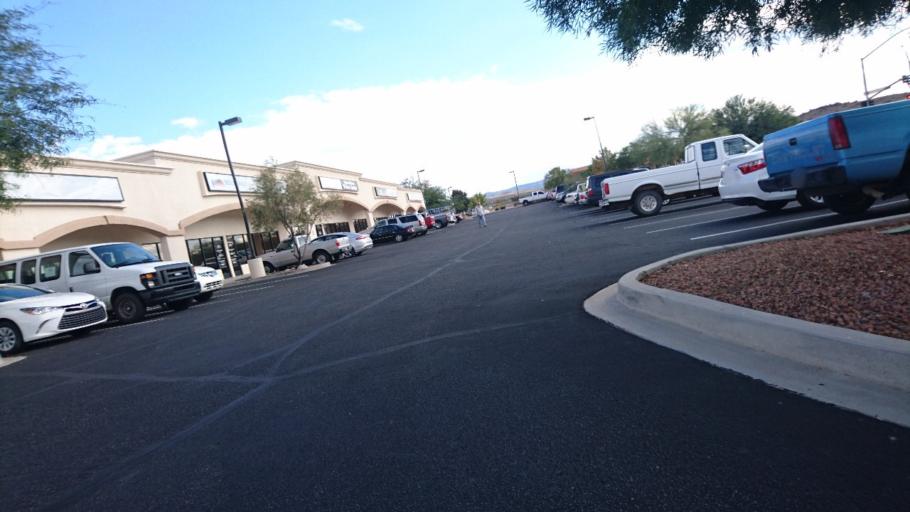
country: US
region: Arizona
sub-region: Mohave County
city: Kingman
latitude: 35.1936
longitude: -114.0268
